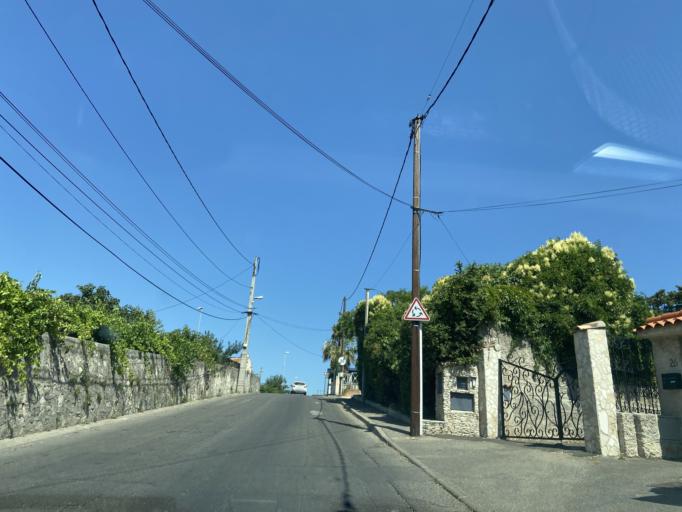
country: FR
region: Provence-Alpes-Cote d'Azur
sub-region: Departement des Bouches-du-Rhone
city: Plan-de-Cuques
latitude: 43.3386
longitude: 5.4509
